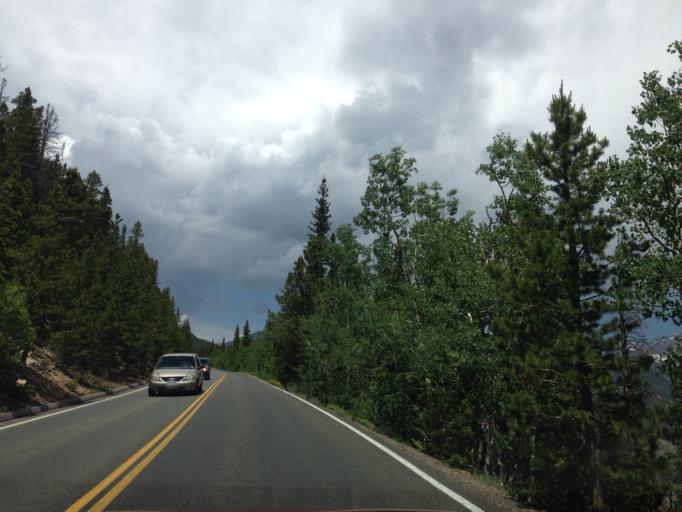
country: US
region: Colorado
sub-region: Larimer County
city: Estes Park
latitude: 40.3933
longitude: -105.6394
